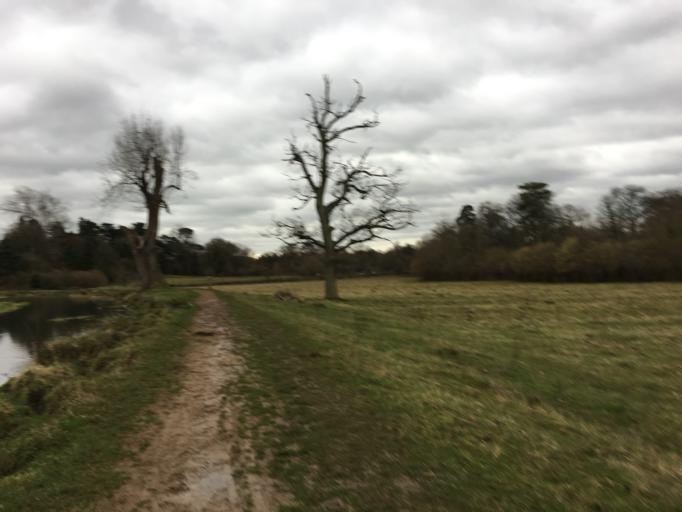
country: GB
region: England
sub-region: Warwickshire
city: Rugby
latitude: 52.3966
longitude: -1.2582
